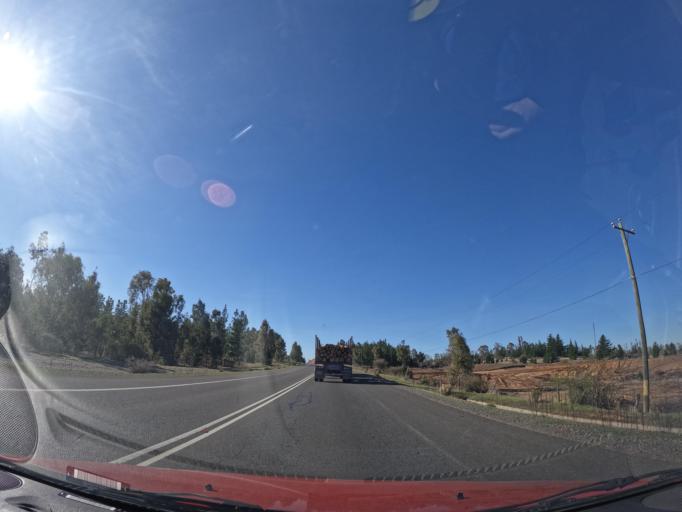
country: CL
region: Maule
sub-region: Provincia de Cauquenes
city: Cauquenes
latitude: -35.9303
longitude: -72.1881
